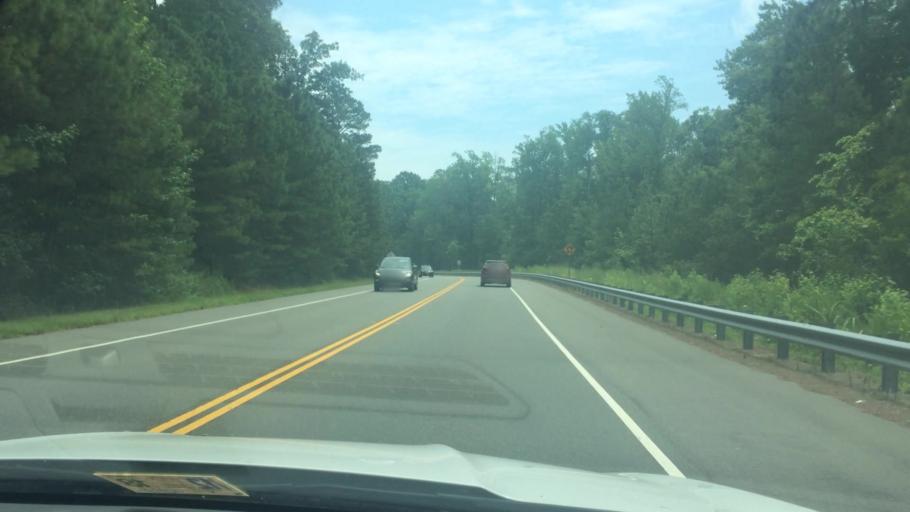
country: US
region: Virginia
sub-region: James City County
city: Williamsburg
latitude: 37.2665
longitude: -76.7700
